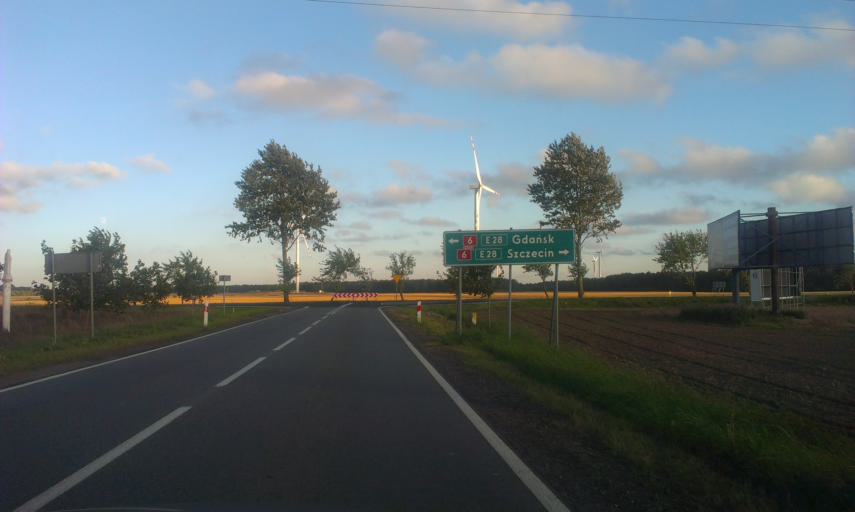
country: PL
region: West Pomeranian Voivodeship
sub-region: Powiat slawienski
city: Slawno
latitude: 54.3262
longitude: 16.5566
